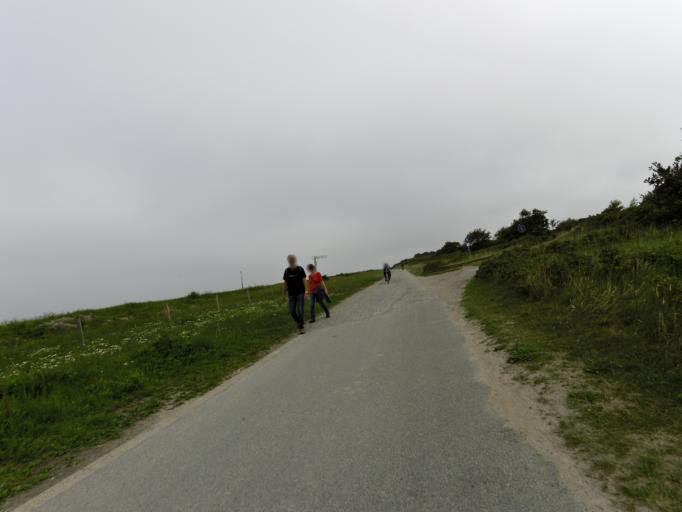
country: DE
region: Lower Saxony
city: Nordholz
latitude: 53.8685
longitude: 8.6025
